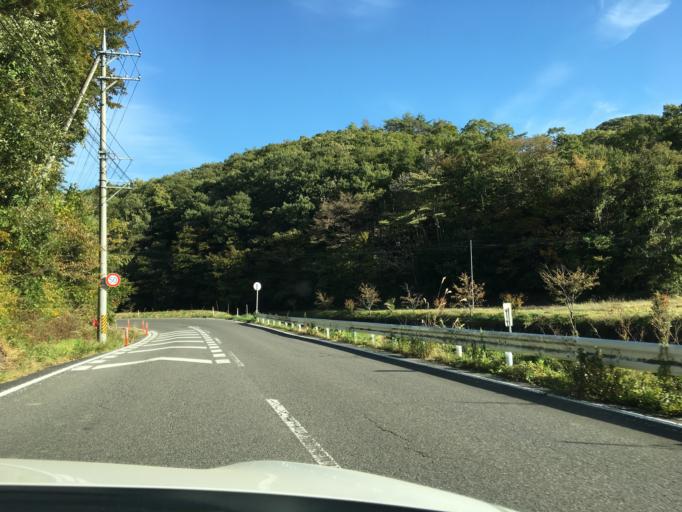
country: JP
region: Fukushima
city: Funehikimachi-funehiki
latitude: 37.3161
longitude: 140.6042
